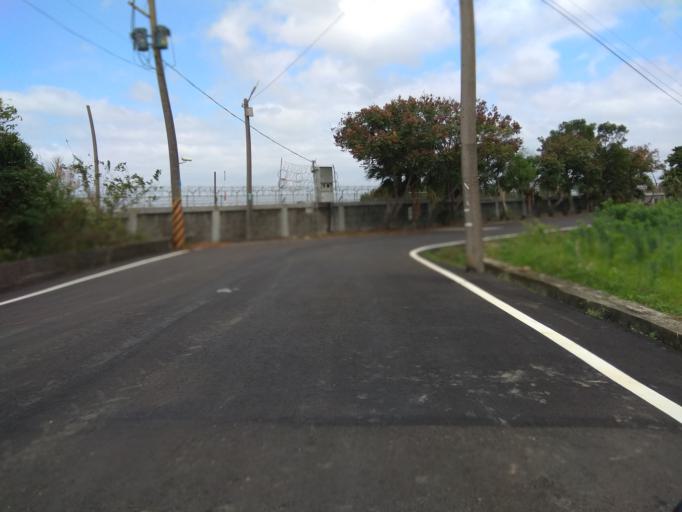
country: TW
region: Taiwan
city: Taoyuan City
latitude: 25.0637
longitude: 121.2309
